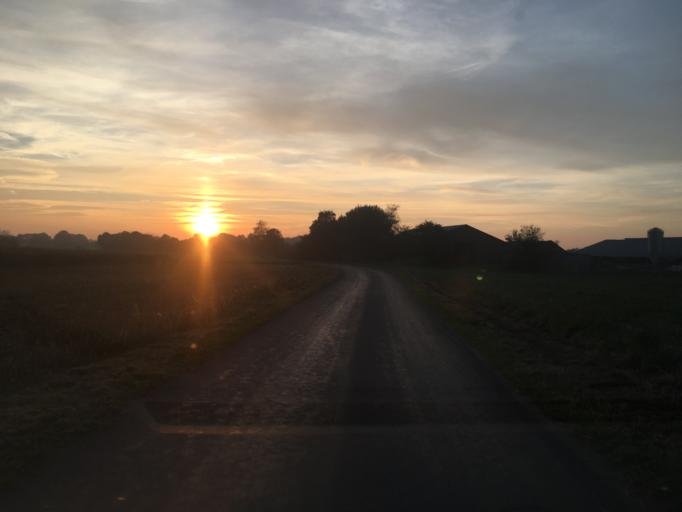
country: DE
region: Schleswig-Holstein
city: Bramstedtlund
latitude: 54.9840
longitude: 9.0743
